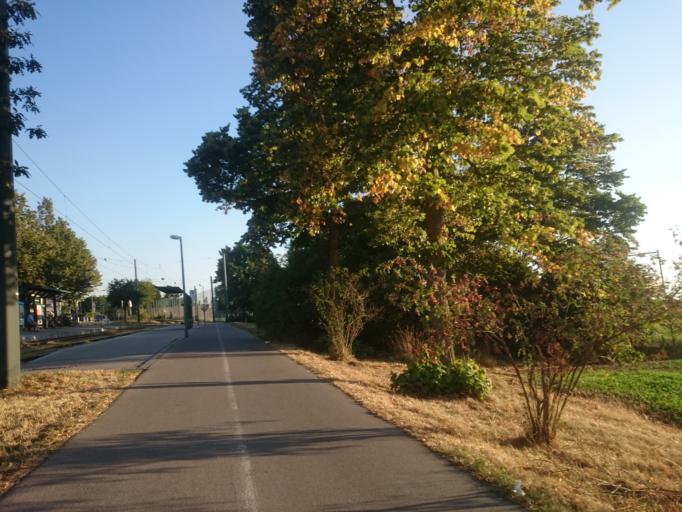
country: DE
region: Bavaria
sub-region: Swabia
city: Konigsbrunn
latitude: 48.3145
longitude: 10.8943
